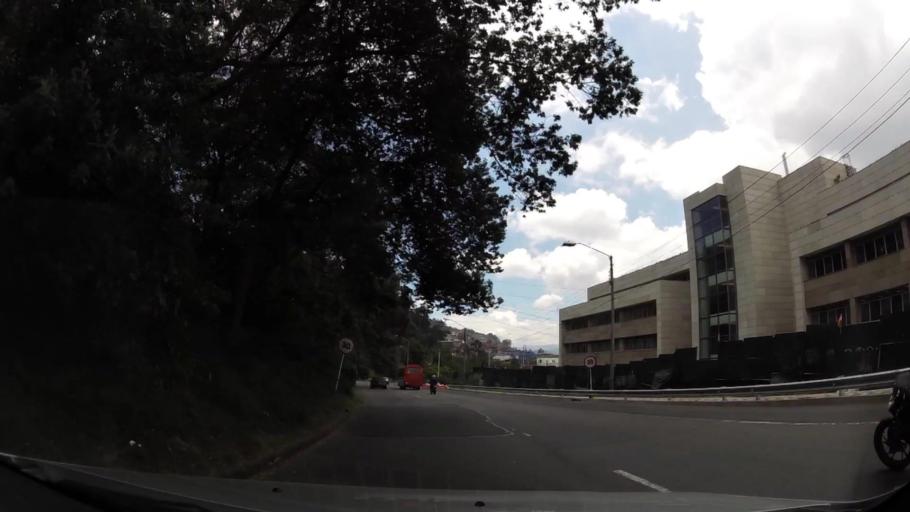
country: CO
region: Bogota D.C.
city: Bogota
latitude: 4.5965
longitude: -74.0669
